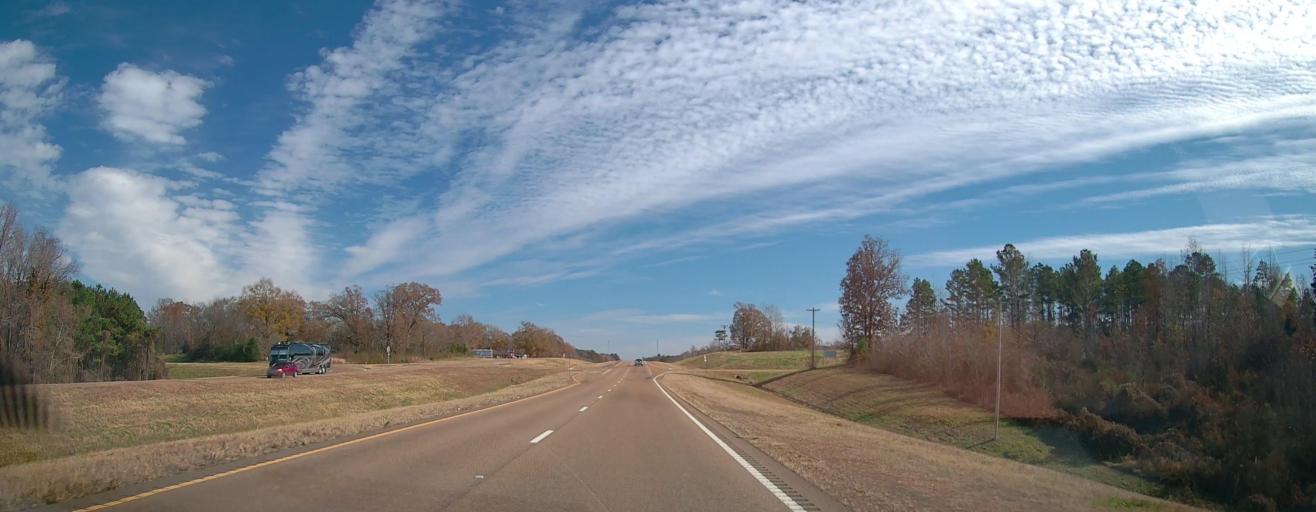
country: US
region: Mississippi
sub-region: Benton County
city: Ashland
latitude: 34.9457
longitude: -89.1734
